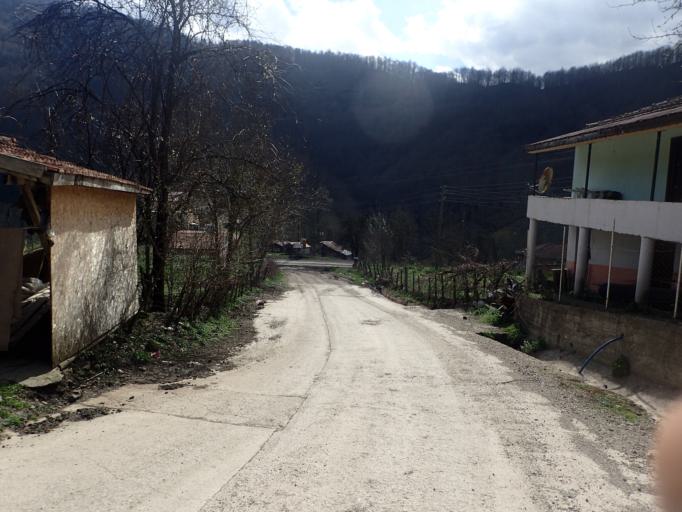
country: TR
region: Ordu
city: Kumru
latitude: 40.8018
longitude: 37.1881
